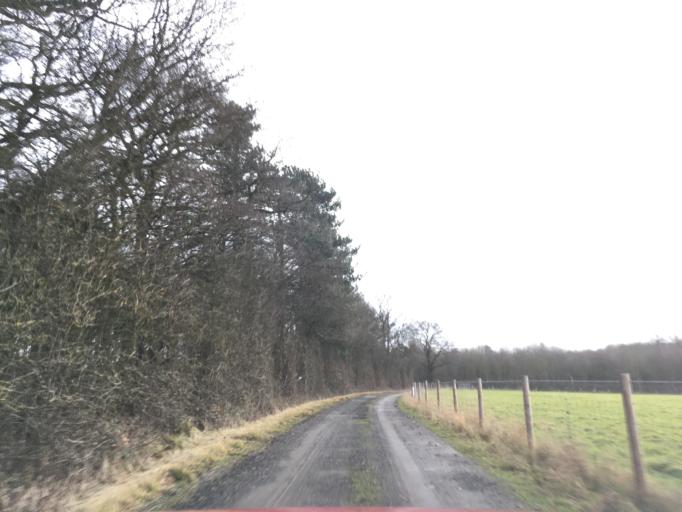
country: GB
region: England
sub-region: Nottinghamshire
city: Gotham
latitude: 52.8462
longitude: -1.2003
